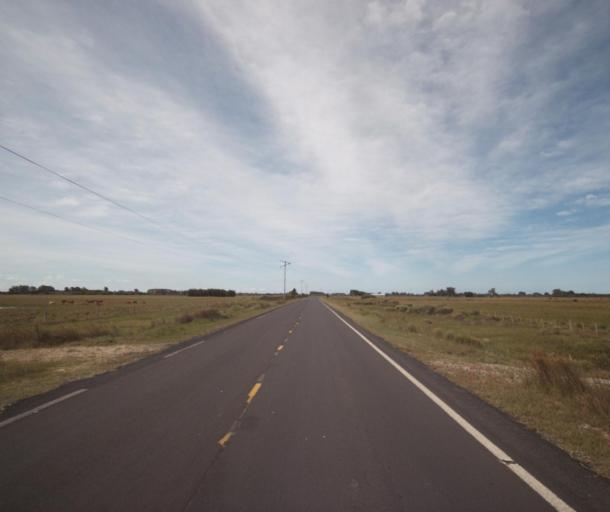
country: BR
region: Rio Grande do Sul
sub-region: Rio Grande
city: Rio Grande
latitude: -31.9304
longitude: -51.9609
